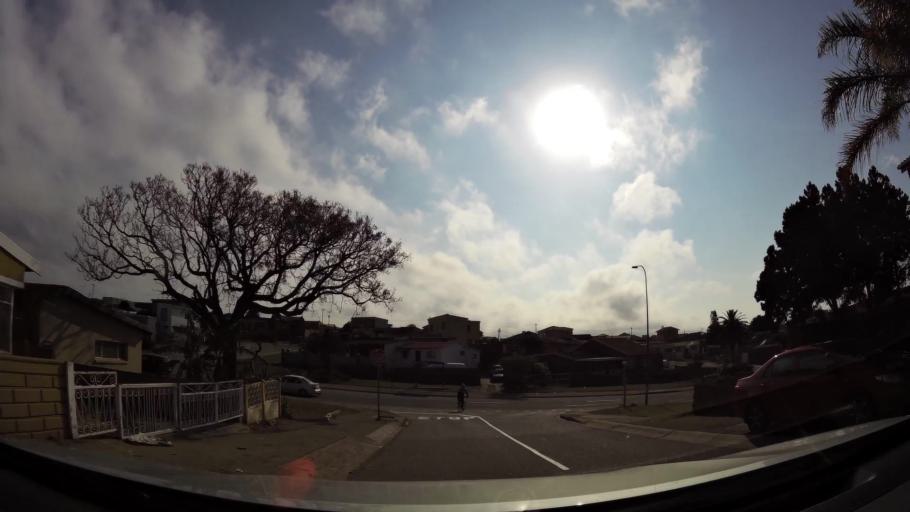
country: ZA
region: Eastern Cape
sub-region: Nelson Mandela Bay Metropolitan Municipality
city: Port Elizabeth
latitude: -33.9247
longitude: 25.5353
